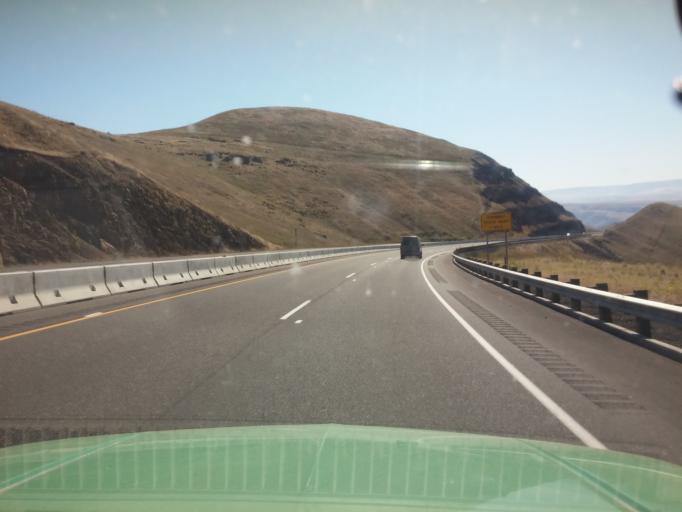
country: US
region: Idaho
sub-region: Nez Perce County
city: Lewiston
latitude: 46.4629
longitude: -116.9854
